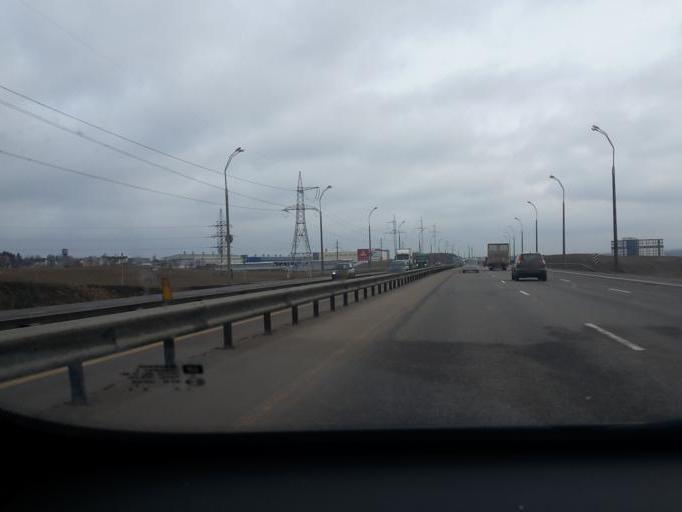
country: BY
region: Minsk
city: Zhdanovichy
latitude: 53.9278
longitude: 27.4191
